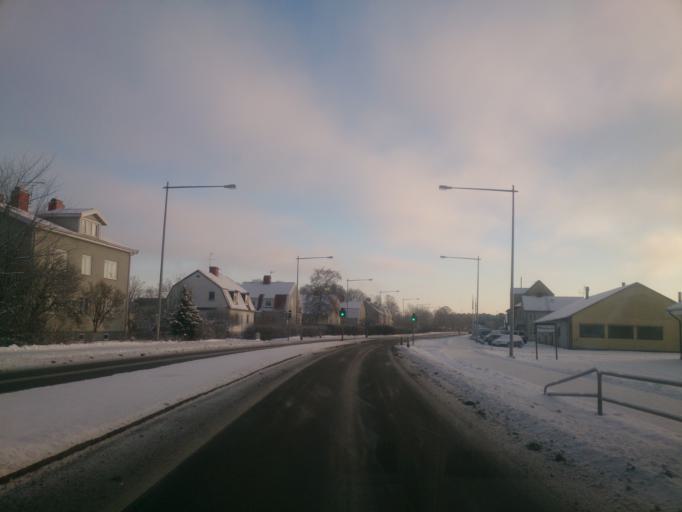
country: SE
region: OEstergoetland
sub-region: Soderkopings Kommun
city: Soederkoeping
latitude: 58.4782
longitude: 16.3281
